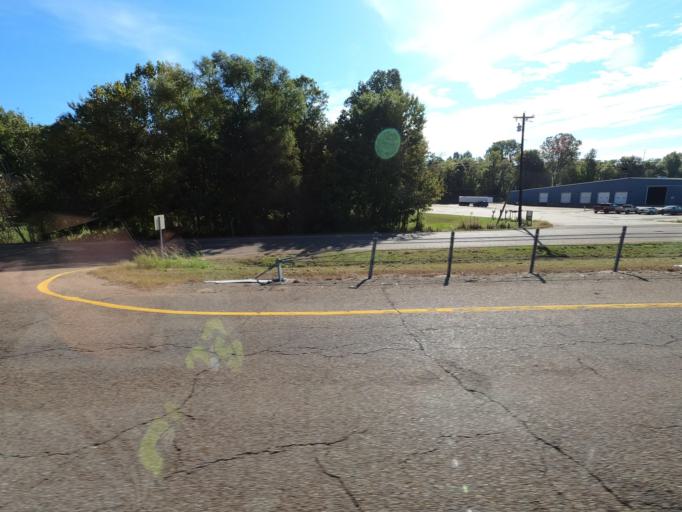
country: US
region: Tennessee
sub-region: Tipton County
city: Brighton
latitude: 35.4959
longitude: -89.7230
